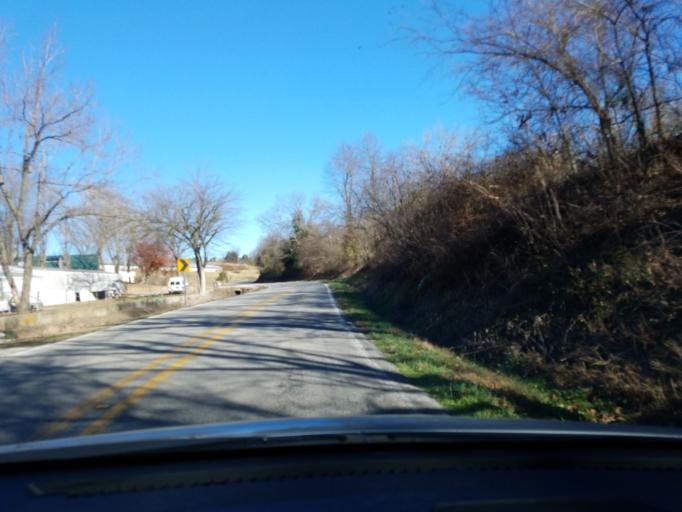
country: US
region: Missouri
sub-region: Stone County
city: Kimberling City
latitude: 36.4885
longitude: -93.4052
